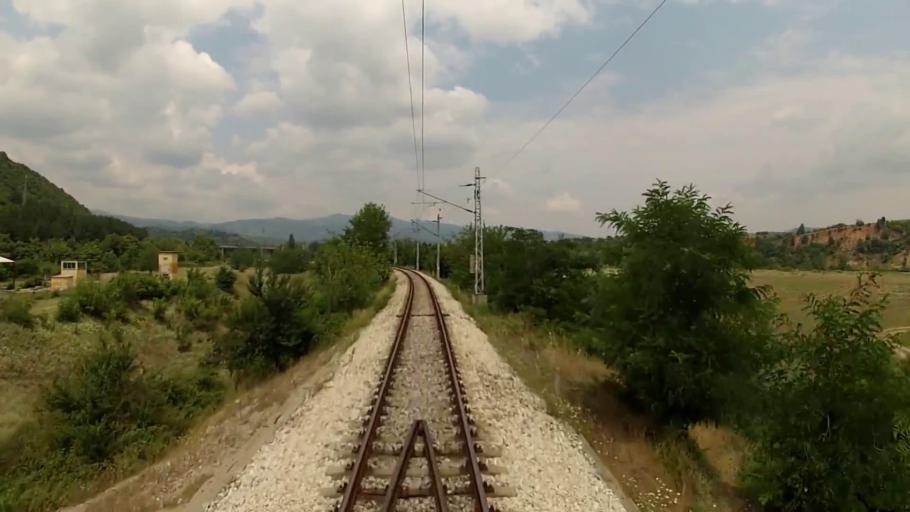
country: BG
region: Blagoevgrad
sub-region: Obshtina Kresna
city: Stara Kresna
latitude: 41.8383
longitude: 23.1522
